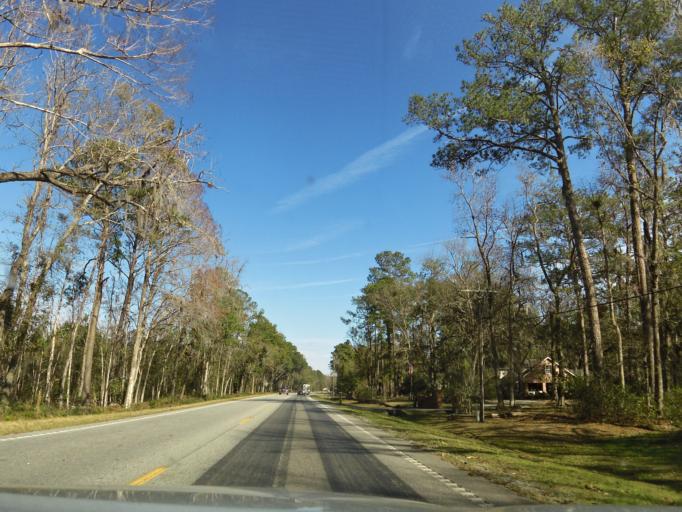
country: US
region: Georgia
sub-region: Glynn County
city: Dock Junction
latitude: 31.2713
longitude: -81.5829
